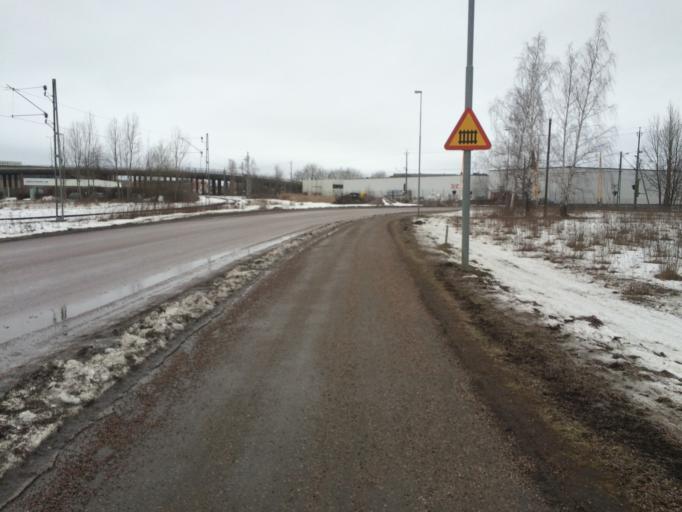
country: SE
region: Vaestmanland
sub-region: Kopings Kommun
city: Koping
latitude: 59.5075
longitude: 15.9972
